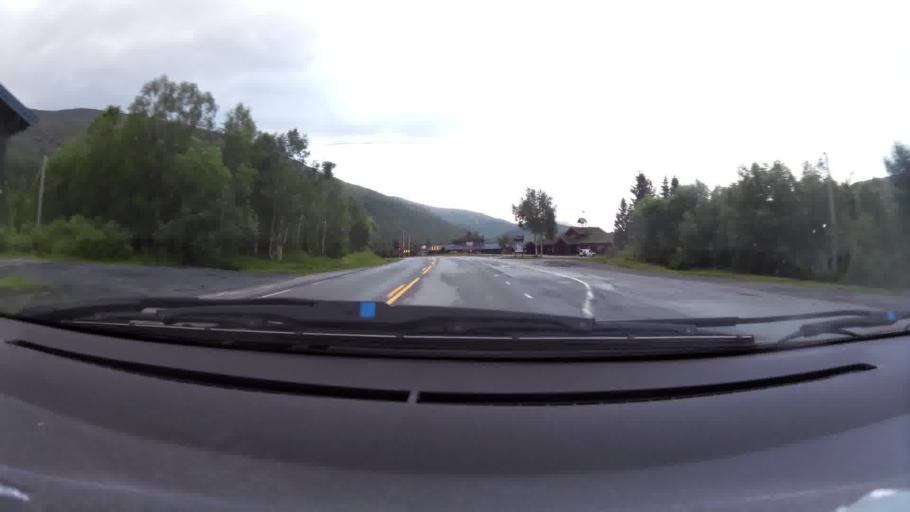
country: NO
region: More og Romsdal
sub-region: Molde
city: Hjelset
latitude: 62.8001
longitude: 7.3291
